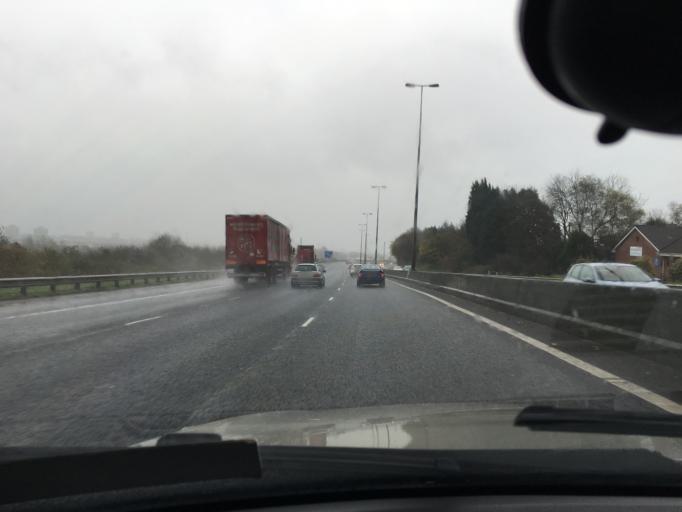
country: GB
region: Northern Ireland
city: Carnmoney
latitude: 54.6627
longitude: -5.9440
